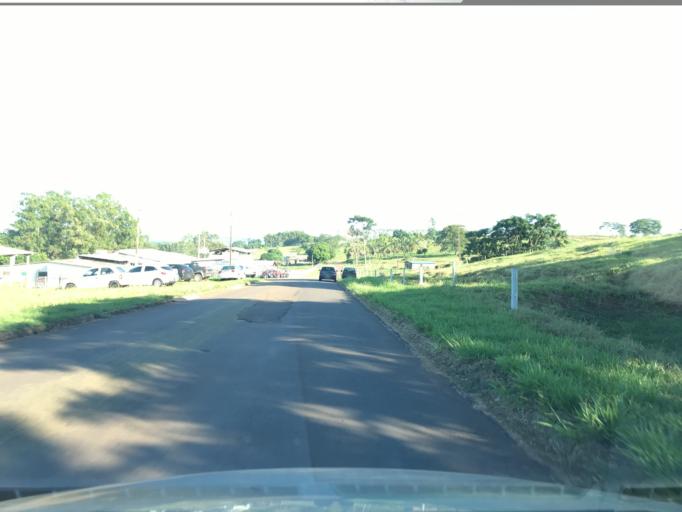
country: BR
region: Parana
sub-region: Ipora
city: Ipora
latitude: -23.9941
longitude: -53.7079
